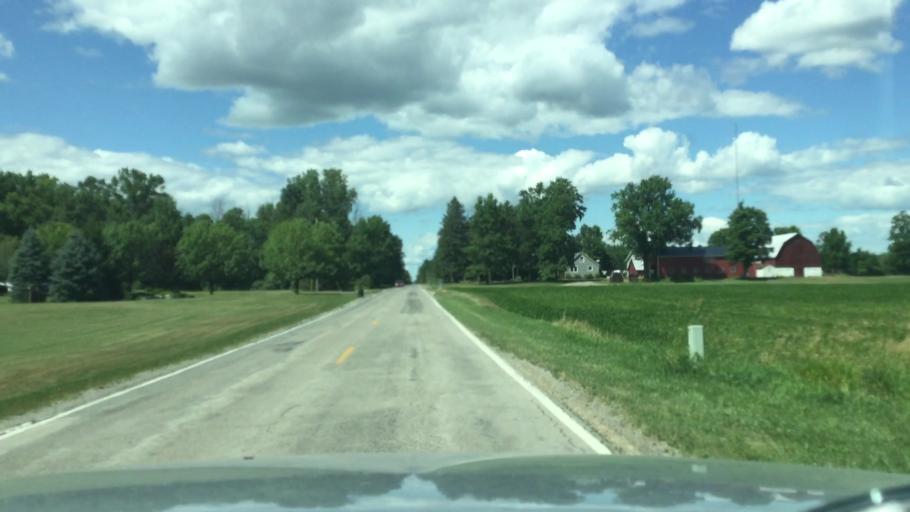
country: US
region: Michigan
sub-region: Saginaw County
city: Hemlock
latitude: 43.3721
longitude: -84.1901
